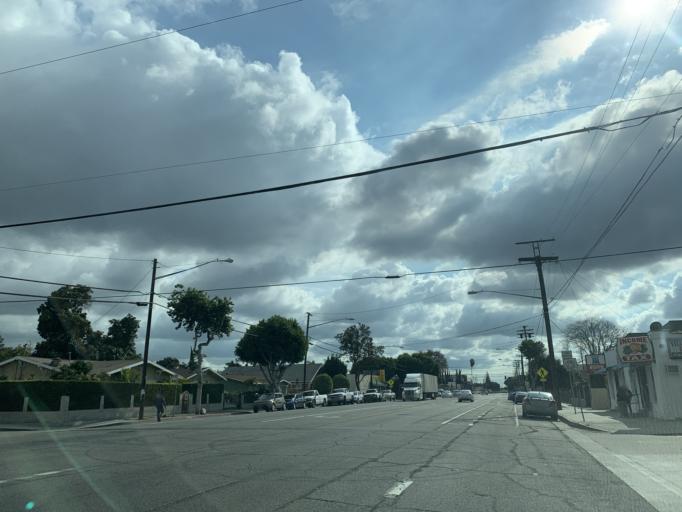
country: US
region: California
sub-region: Los Angeles County
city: Huntington Park
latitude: 33.9840
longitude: -118.2413
